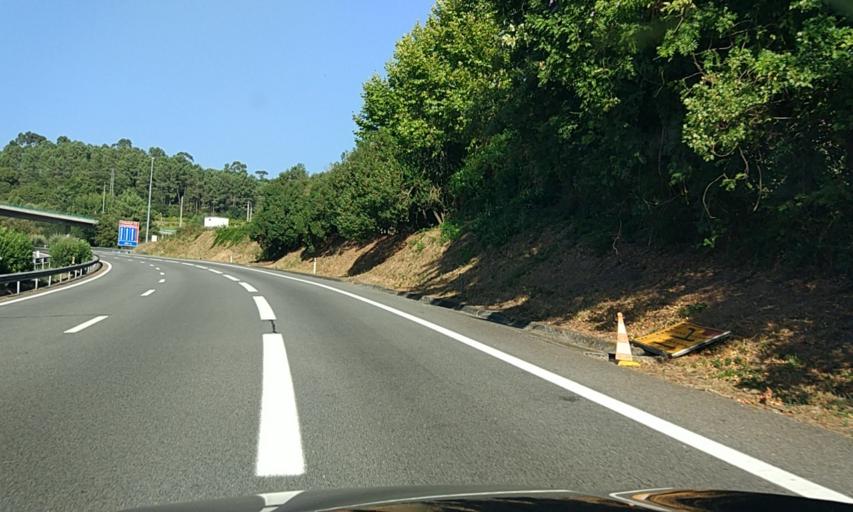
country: PT
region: Porto
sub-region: Marco de Canaveses
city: Marco de Canavezes
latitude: 41.2256
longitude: -8.1535
